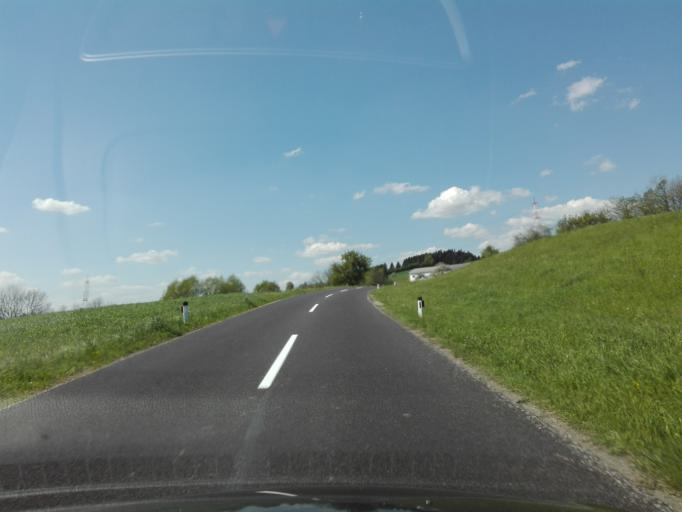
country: AT
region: Upper Austria
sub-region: Politischer Bezirk Rohrbach
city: Kleinzell im Muehlkreis
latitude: 48.3585
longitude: 13.9376
